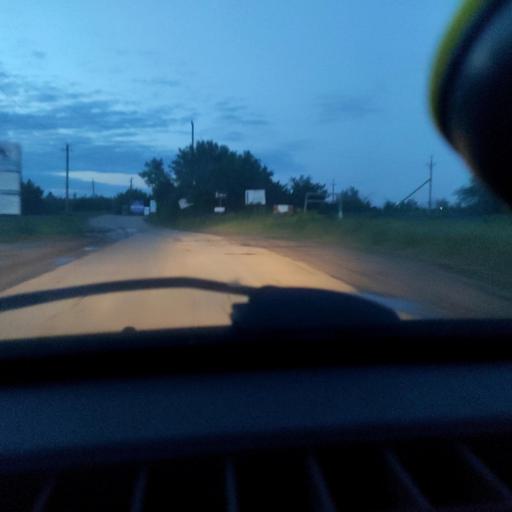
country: RU
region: Samara
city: Tol'yatti
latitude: 53.5680
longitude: 49.3602
